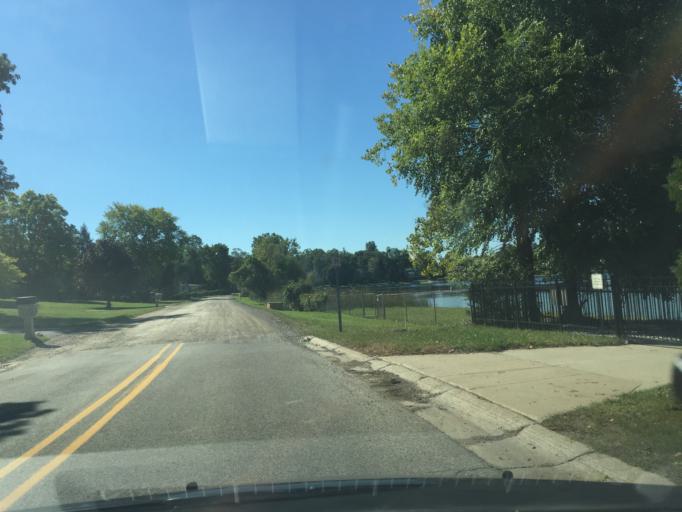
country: US
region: Michigan
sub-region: Oakland County
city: Sylvan Lake
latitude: 42.6100
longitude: -83.3077
